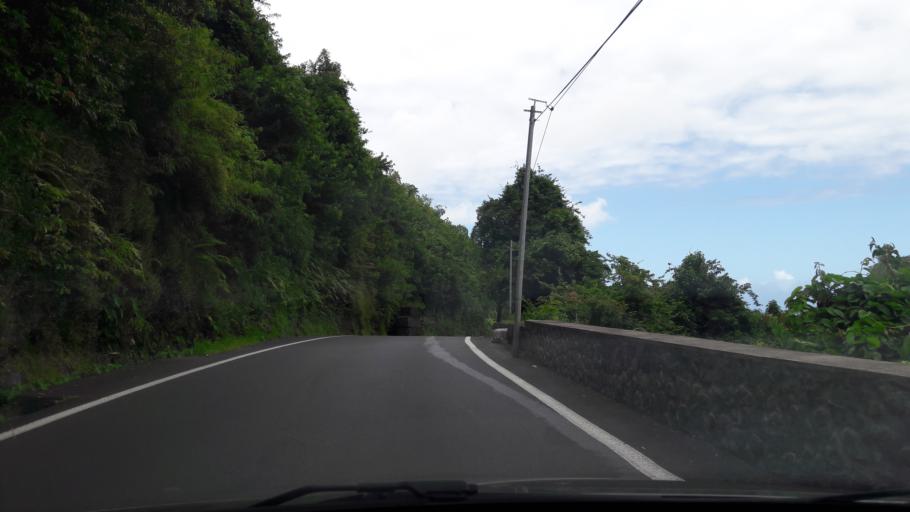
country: RE
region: Reunion
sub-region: Reunion
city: Saint-Andre
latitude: -20.9858
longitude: 55.6246
